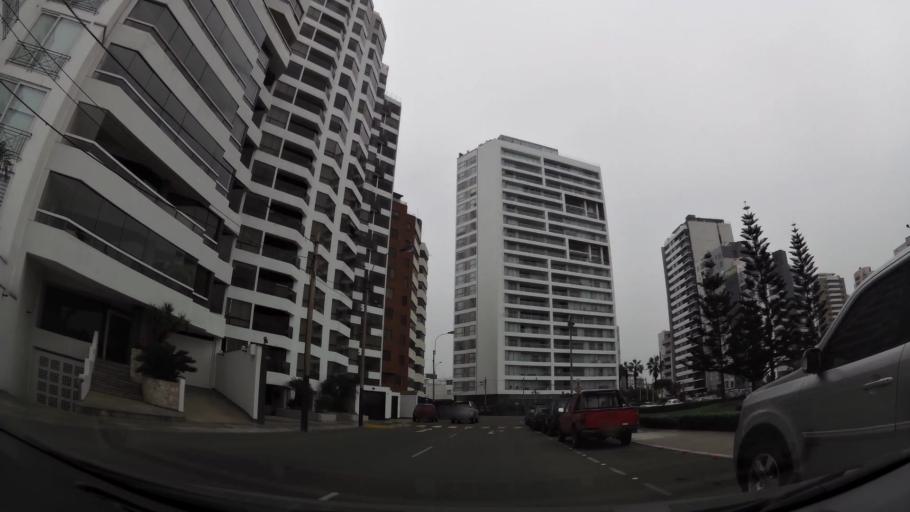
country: PE
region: Lima
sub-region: Lima
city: San Isidro
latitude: -12.1185
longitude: -77.0446
